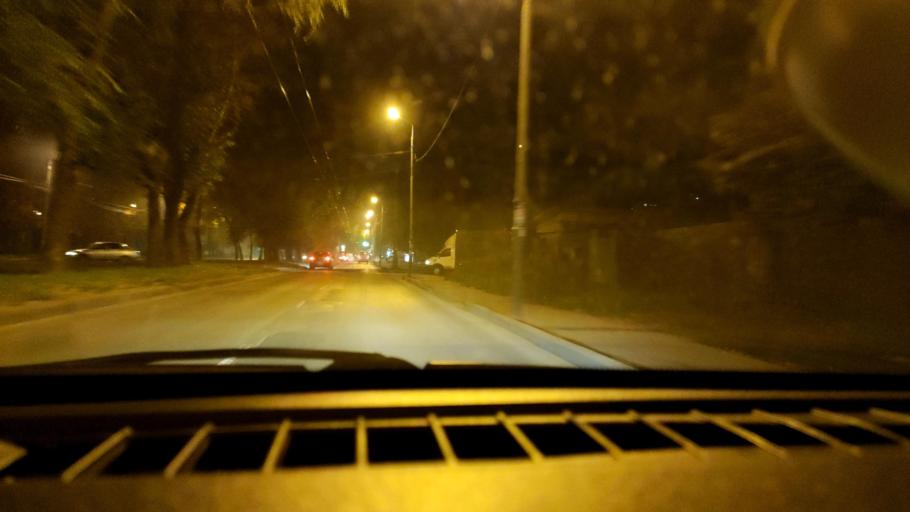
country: RU
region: Samara
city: Samara
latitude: 53.2232
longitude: 50.2516
